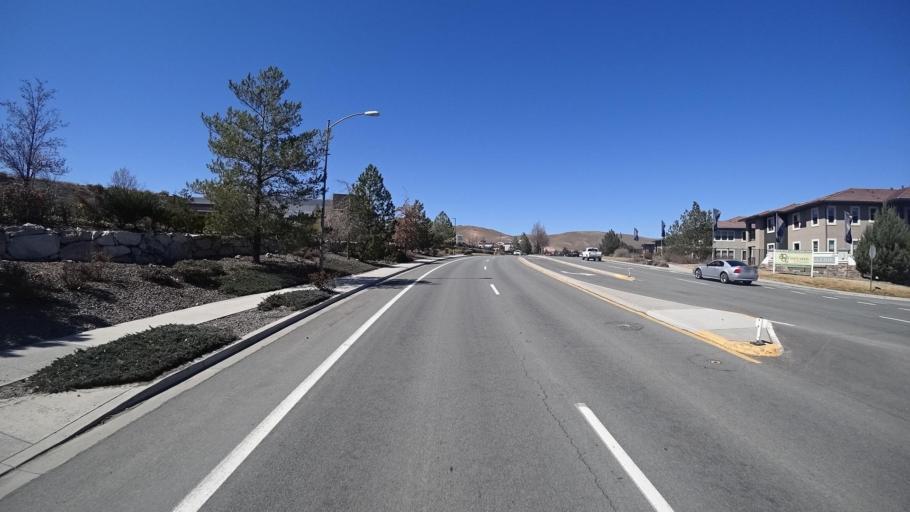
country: US
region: Nevada
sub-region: Washoe County
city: Sparks
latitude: 39.5751
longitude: -119.7373
